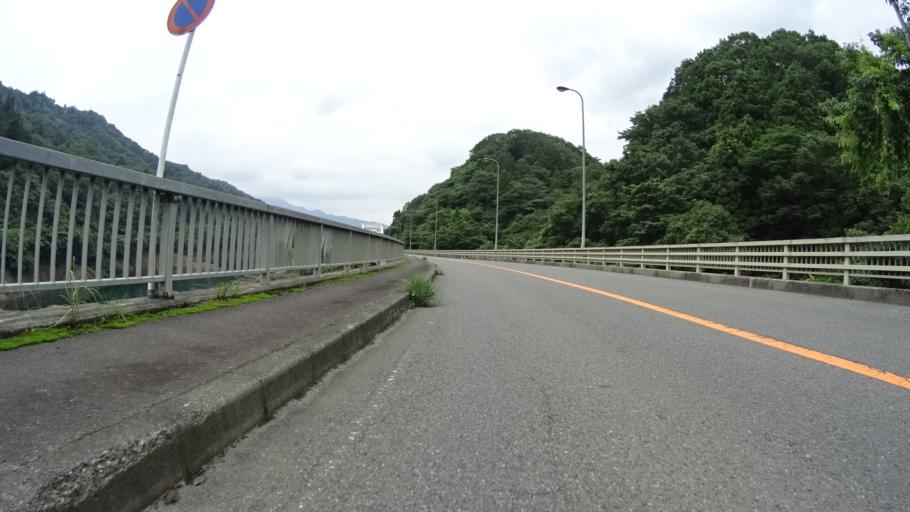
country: JP
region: Kanagawa
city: Atsugi
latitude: 35.5064
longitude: 139.2546
